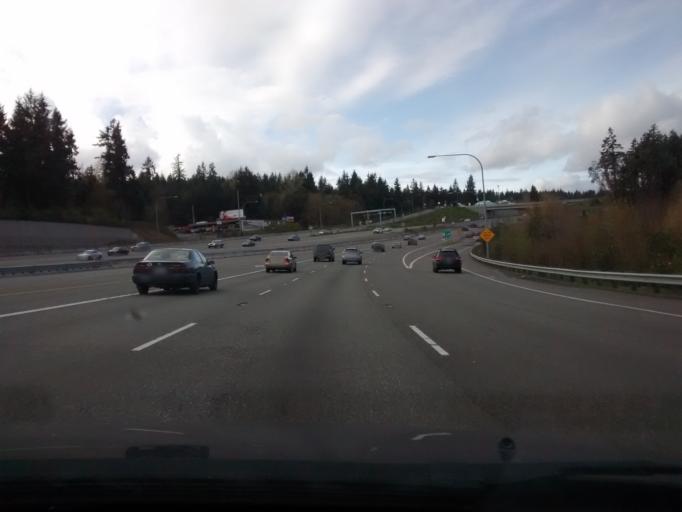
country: US
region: Washington
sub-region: Pierce County
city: Wollochet
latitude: 47.2755
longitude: -122.5593
